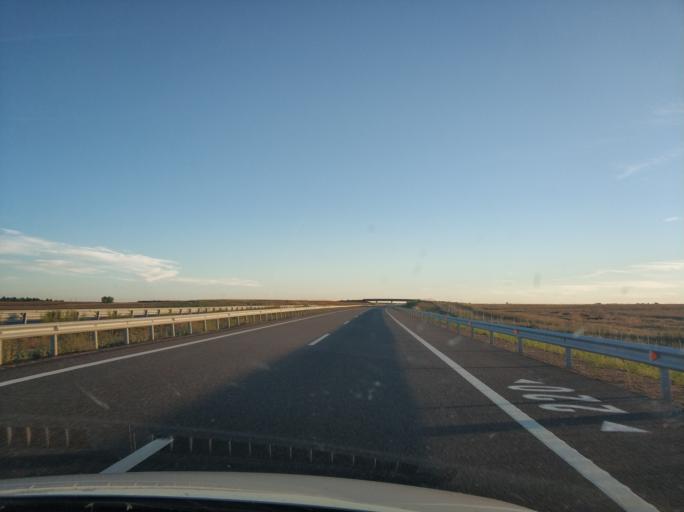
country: ES
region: Castille and Leon
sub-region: Provincia de Zamora
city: Castrogonzalo
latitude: 41.9575
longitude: -5.6147
